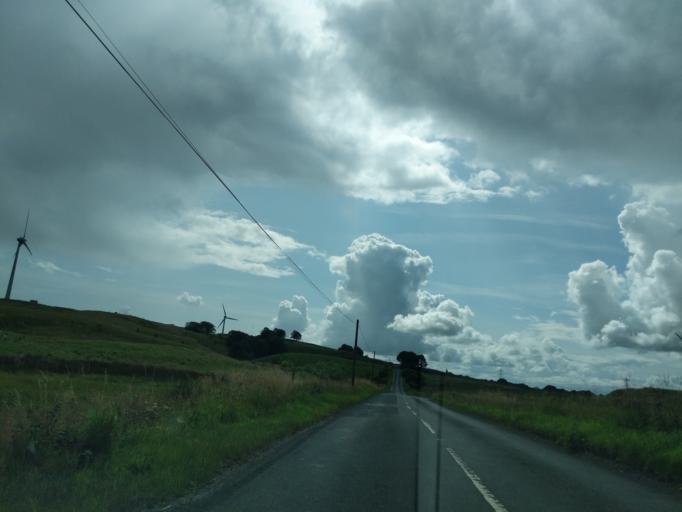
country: GB
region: Scotland
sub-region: East Renfrewshire
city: Neilston
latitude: 55.7534
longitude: -4.4565
